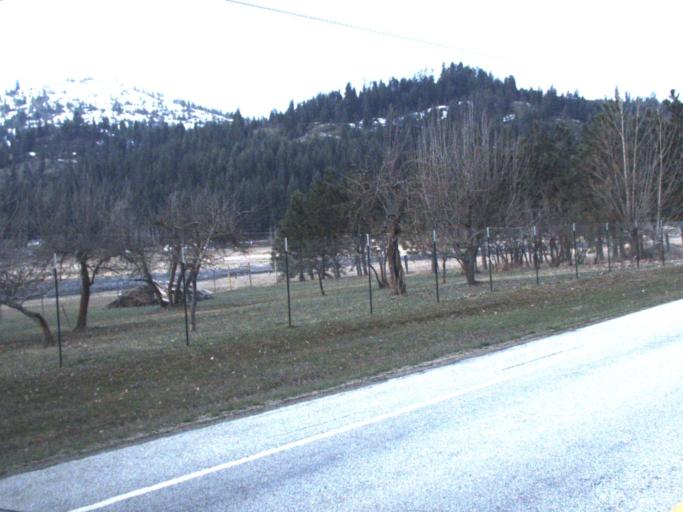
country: US
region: Washington
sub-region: Pend Oreille County
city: Newport
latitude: 48.2310
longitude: -117.1718
